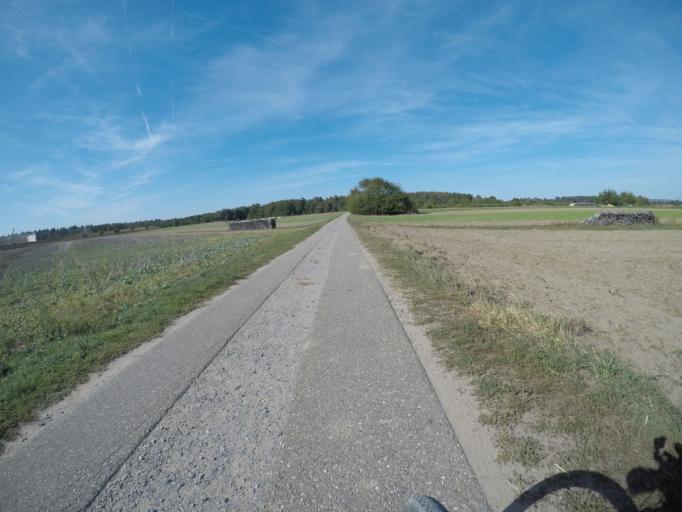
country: DE
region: Baden-Wuerttemberg
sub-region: Karlsruhe Region
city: Kronau
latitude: 49.2272
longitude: 8.6205
